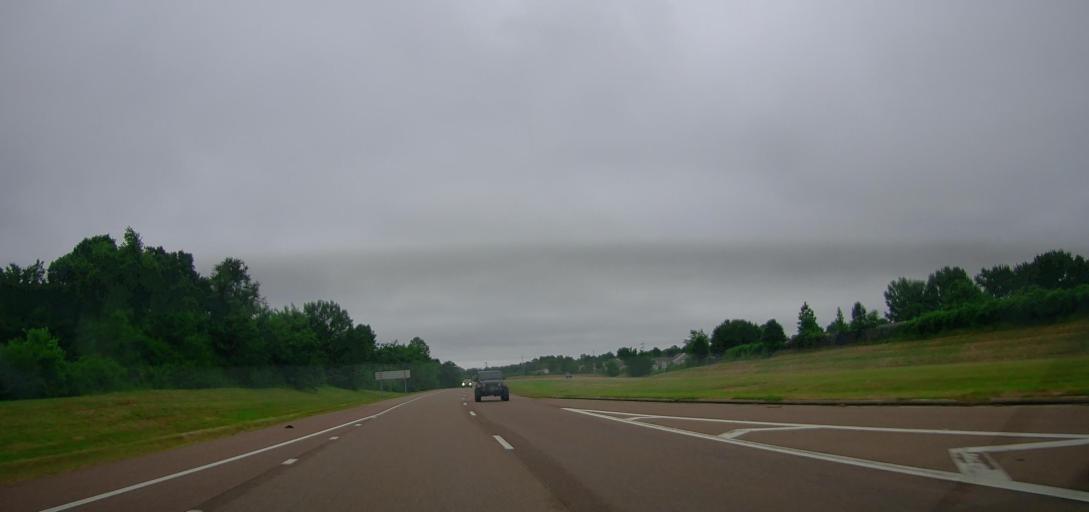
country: US
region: Mississippi
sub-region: De Soto County
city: Olive Branch
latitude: 34.9644
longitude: -89.8006
